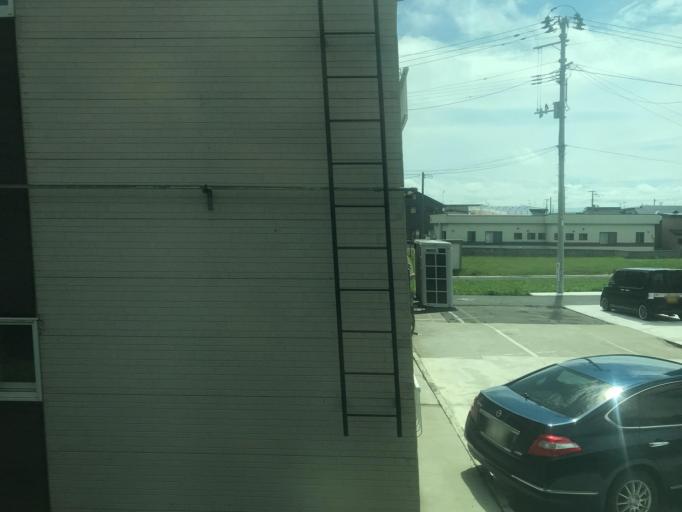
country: JP
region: Aomori
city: Goshogawara
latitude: 40.7999
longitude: 140.4475
